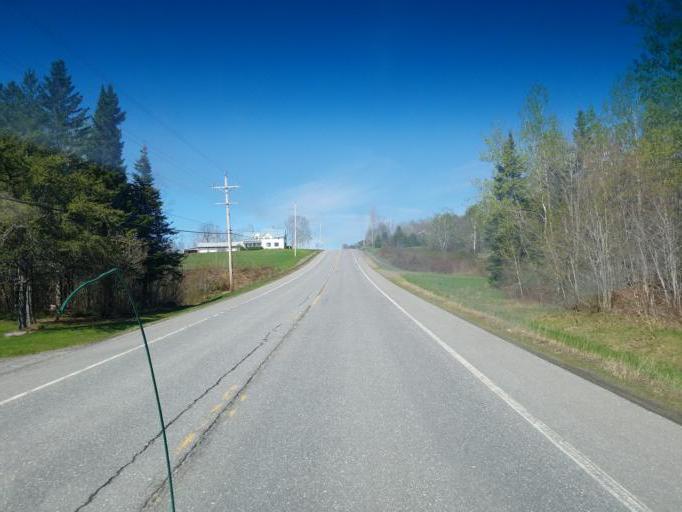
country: US
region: Maine
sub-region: Aroostook County
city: Presque Isle
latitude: 46.6668
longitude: -68.2082
